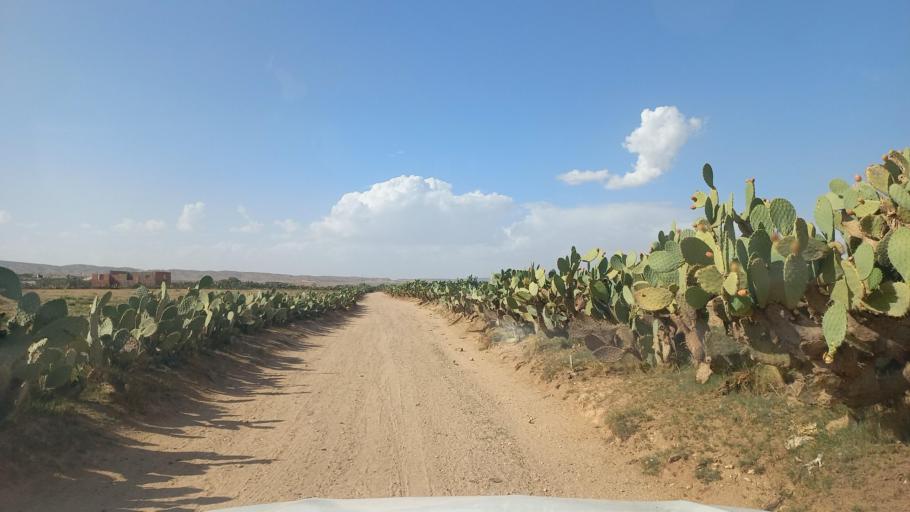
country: TN
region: Al Qasrayn
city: Sbiba
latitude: 35.3141
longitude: 9.0308
